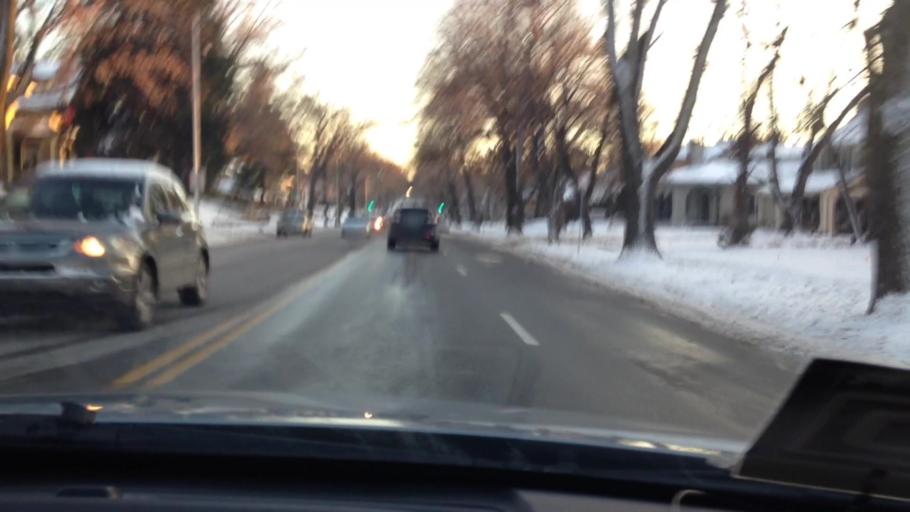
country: US
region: Kansas
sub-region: Johnson County
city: Mission Hills
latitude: 39.0291
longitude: -94.5760
